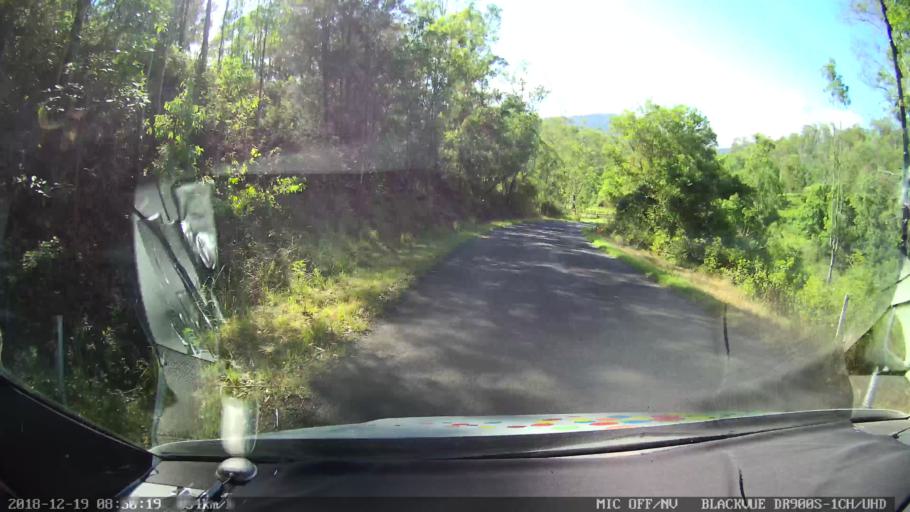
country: AU
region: New South Wales
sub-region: Kyogle
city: Kyogle
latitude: -28.3801
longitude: 152.9755
